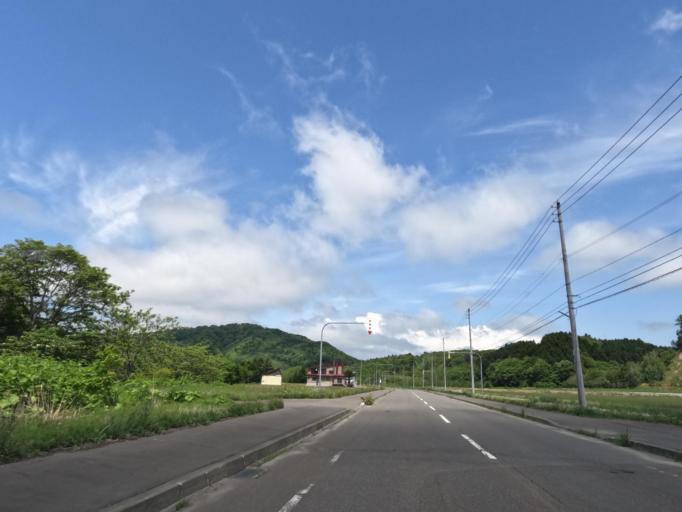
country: JP
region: Hokkaido
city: Tobetsu
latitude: 43.3080
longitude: 141.5557
